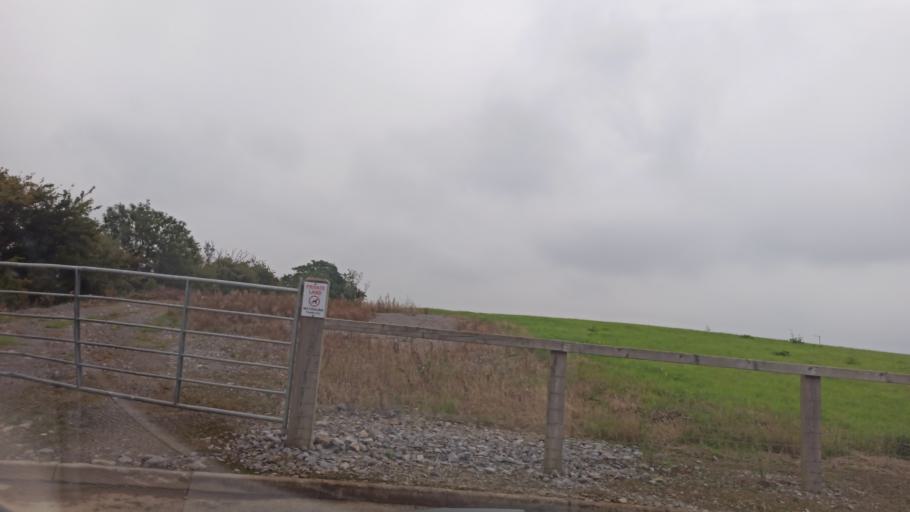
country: IE
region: Munster
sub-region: South Tipperary
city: Cluain Meala
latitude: 52.3749
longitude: -7.7286
